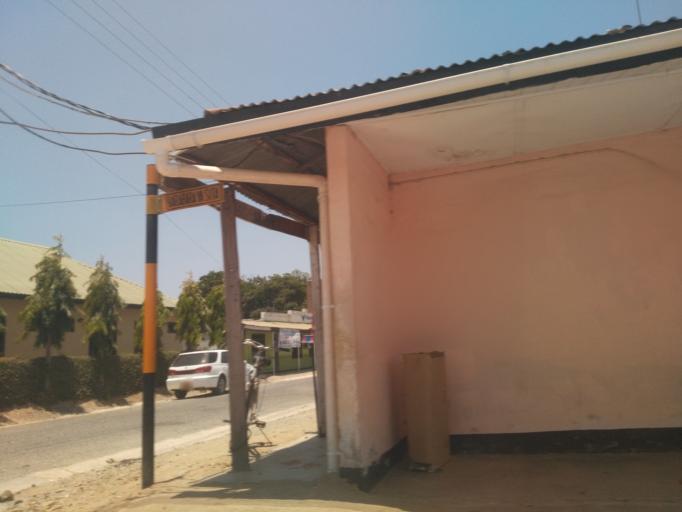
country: TZ
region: Dodoma
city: Dodoma
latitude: -6.1754
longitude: 35.7455
